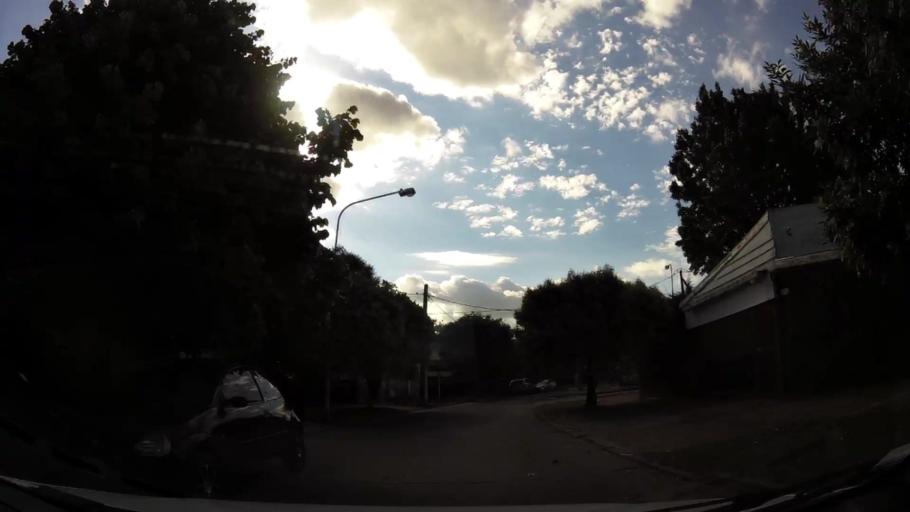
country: AR
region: Buenos Aires
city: San Justo
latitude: -34.6698
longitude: -58.5873
